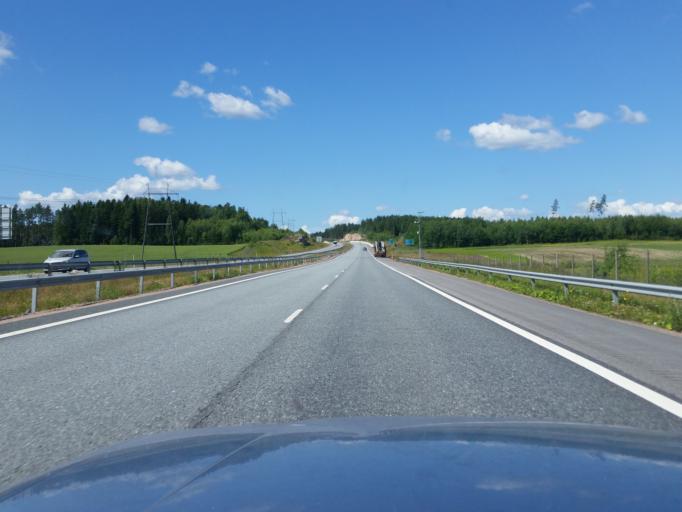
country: FI
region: Varsinais-Suomi
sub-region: Salo
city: Kiikala
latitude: 60.3909
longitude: 23.5734
